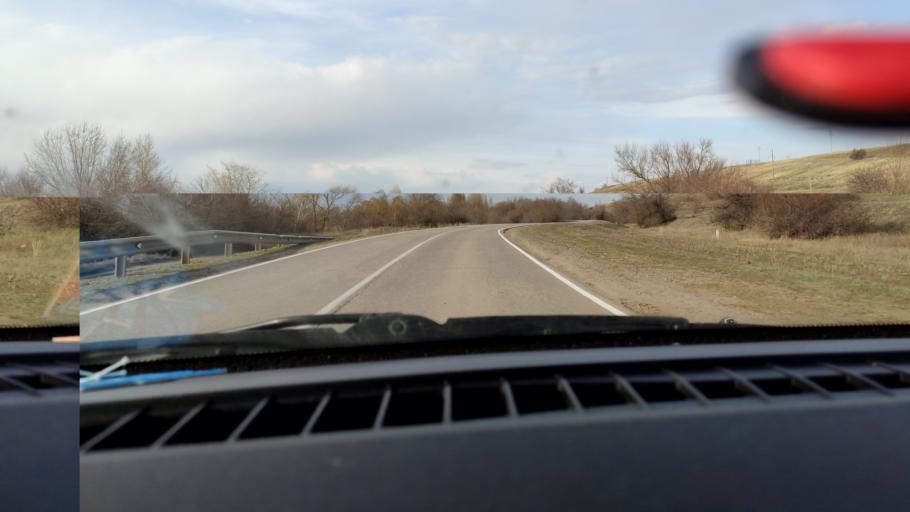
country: RU
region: Saratov
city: Privolzhskiy
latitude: 51.2233
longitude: 45.9203
